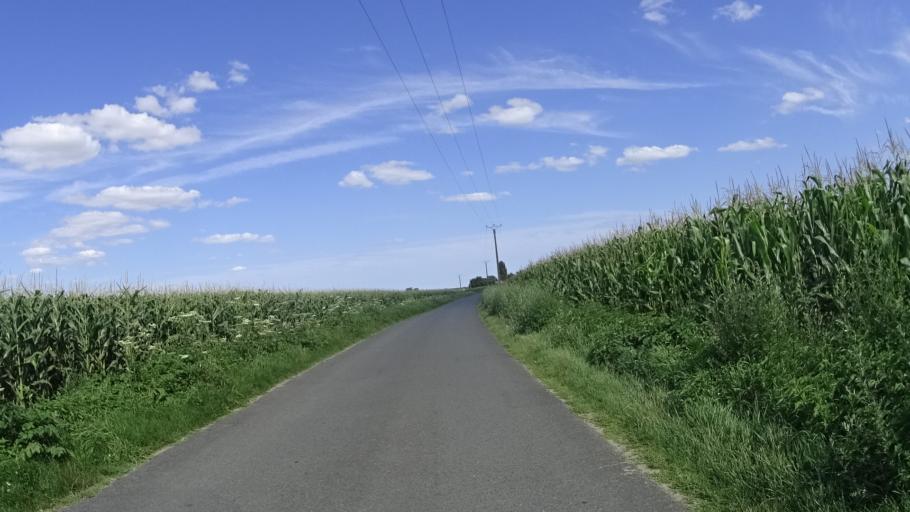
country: FR
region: Centre
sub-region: Departement d'Indre-et-Loire
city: Noizay
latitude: 47.4060
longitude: 0.9051
